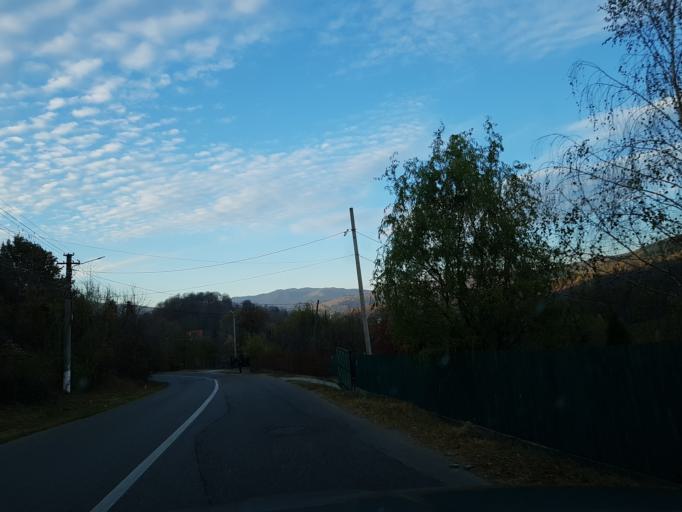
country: RO
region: Prahova
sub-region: Oras Breaza
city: Gura Beliei
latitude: 45.2075
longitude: 25.6494
